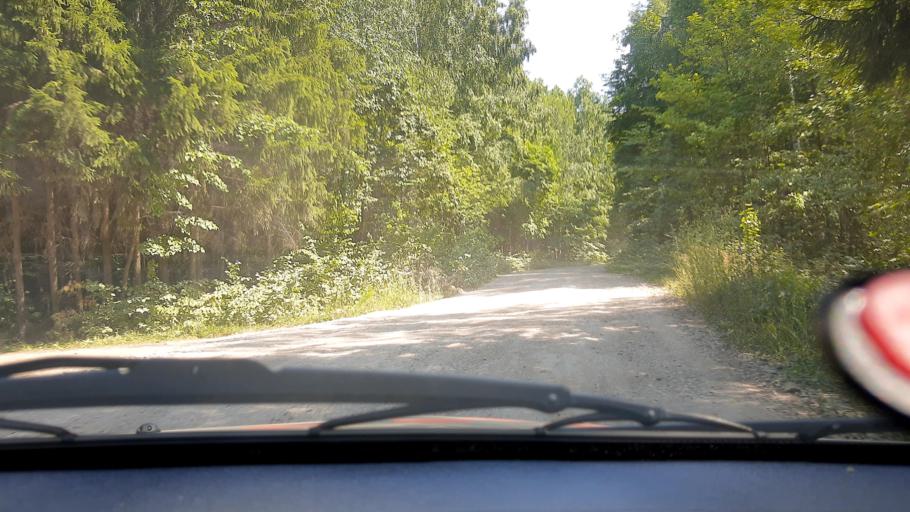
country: RU
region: Bashkortostan
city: Karmaskaly
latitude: 54.3863
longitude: 55.9124
